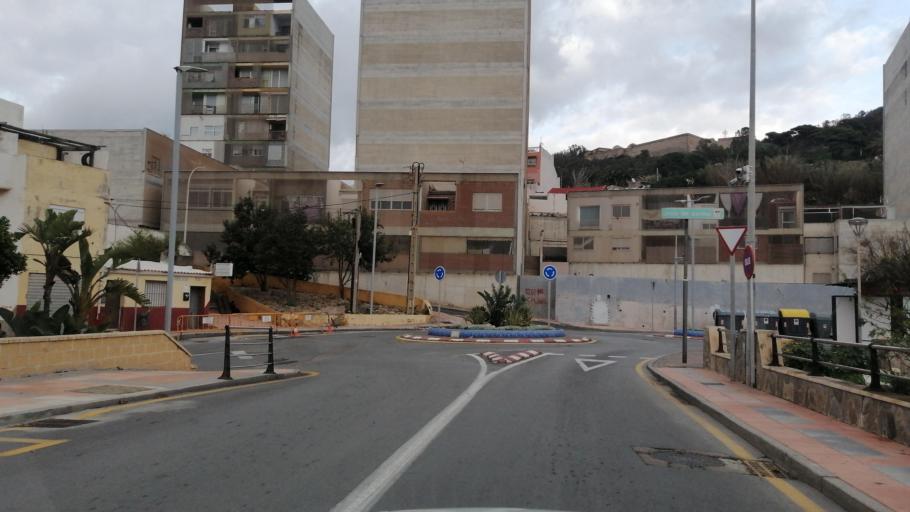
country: ES
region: Ceuta
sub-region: Ceuta
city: Ceuta
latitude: 35.8911
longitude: -5.2975
